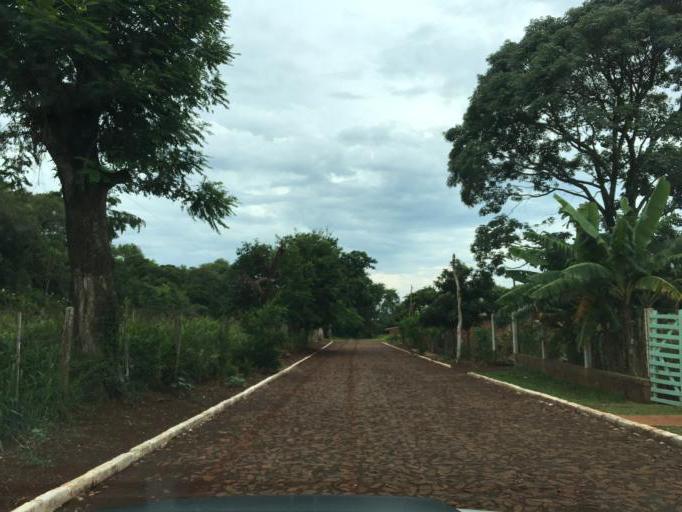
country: PY
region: Alto Parana
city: Ciudad del Este
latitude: -25.4135
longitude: -54.6552
